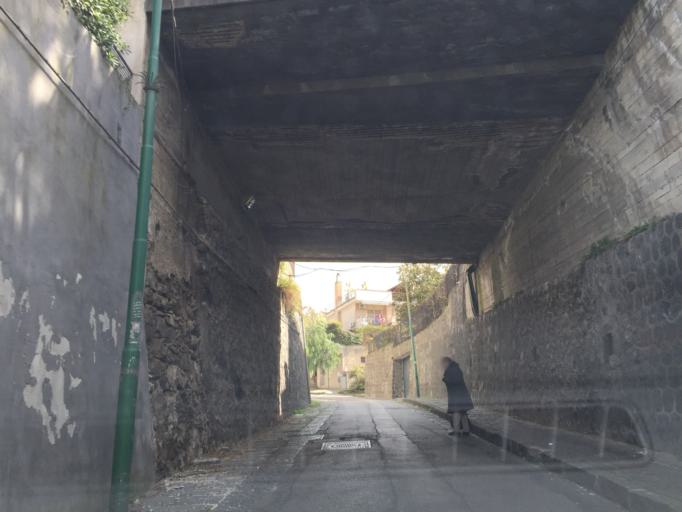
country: IT
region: Campania
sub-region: Provincia di Napoli
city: Massa di Somma
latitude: 40.8423
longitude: 14.3719
